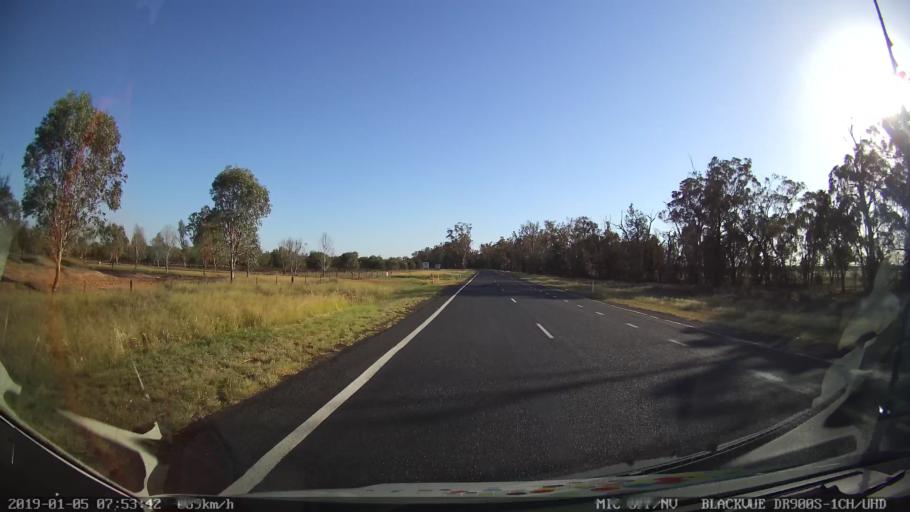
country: AU
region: New South Wales
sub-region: Gilgandra
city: Gilgandra
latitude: -31.7409
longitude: 148.6435
